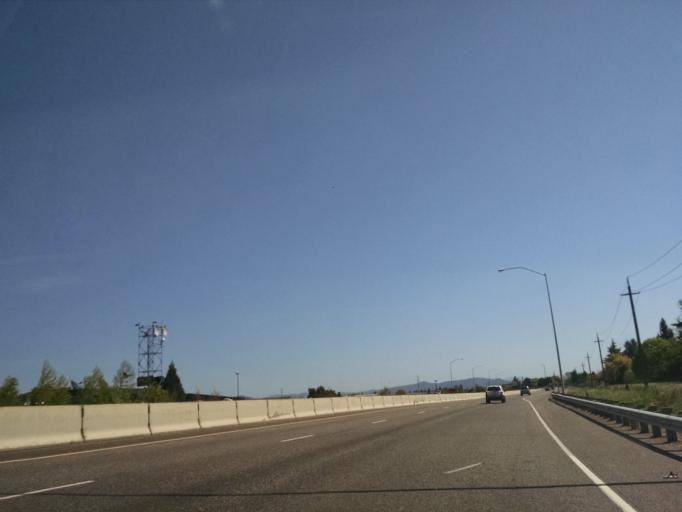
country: US
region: Oregon
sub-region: Lane County
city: Eugene
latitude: 44.0870
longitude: -123.0627
